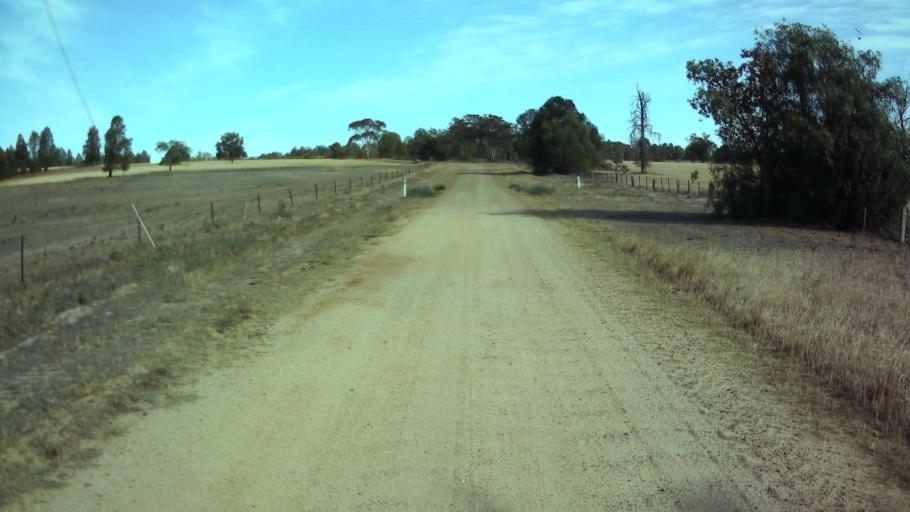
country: AU
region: New South Wales
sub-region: Weddin
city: Grenfell
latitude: -33.7764
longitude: 148.0520
